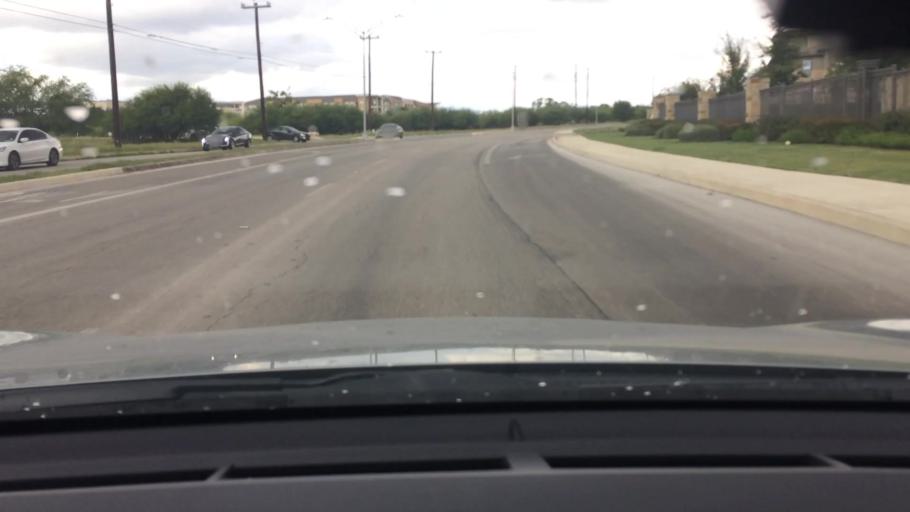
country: US
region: Texas
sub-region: Bexar County
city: Shavano Park
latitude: 29.5806
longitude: -98.5881
